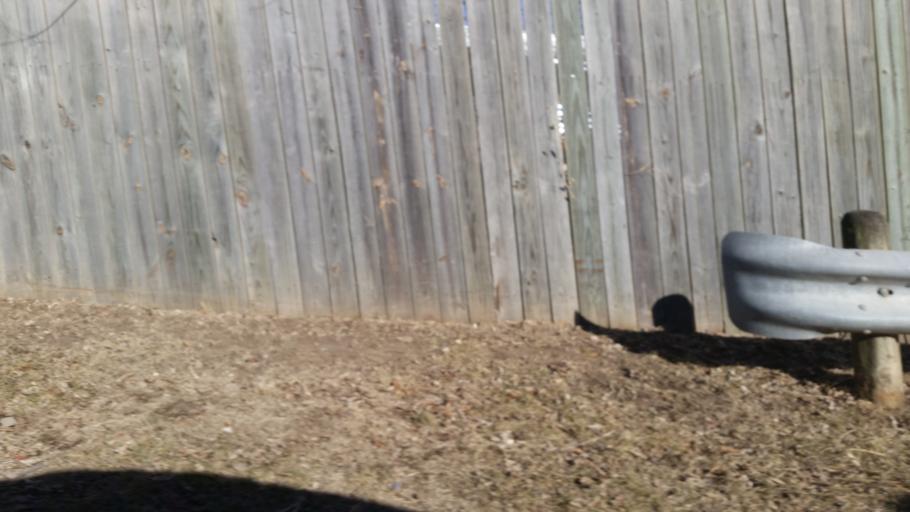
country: US
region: Nebraska
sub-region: Douglas County
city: Omaha
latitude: 41.2221
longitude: -95.9277
